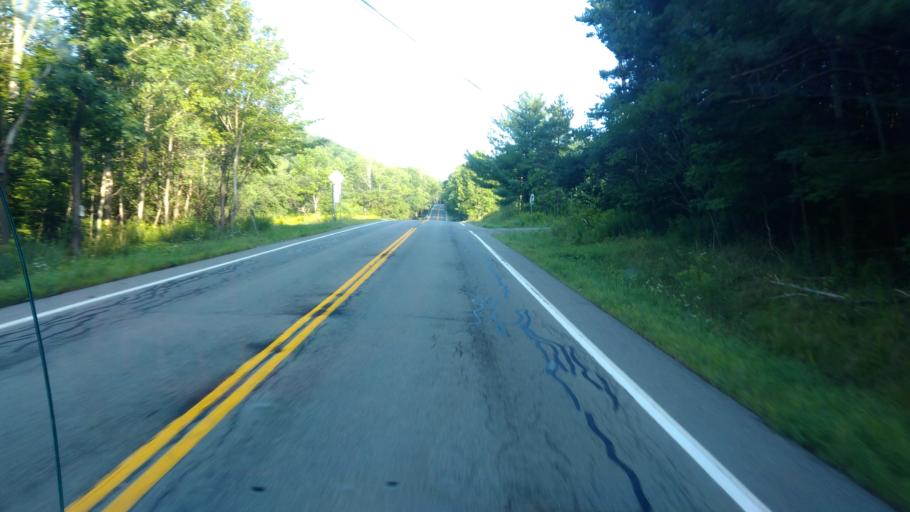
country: US
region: New York
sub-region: Allegany County
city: Andover
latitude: 42.1468
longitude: -77.6856
